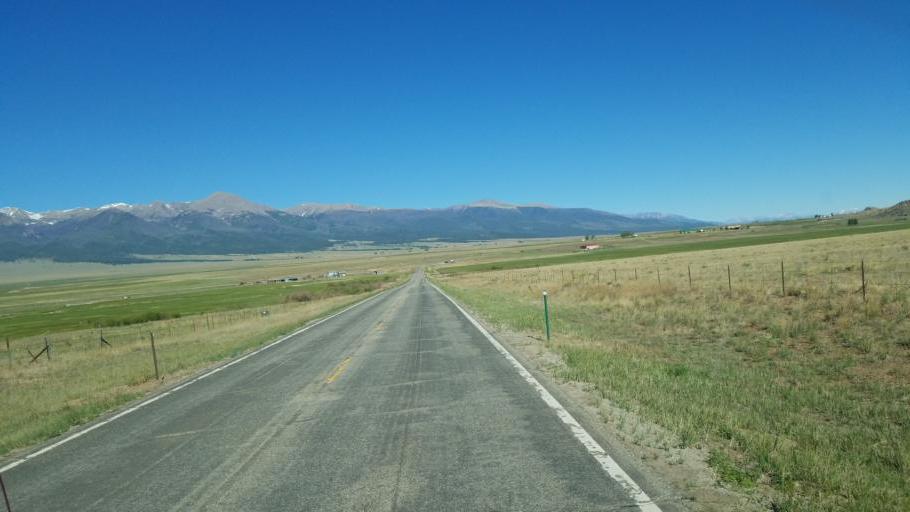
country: US
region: Colorado
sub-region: Custer County
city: Westcliffe
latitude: 38.1684
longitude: -105.4917
